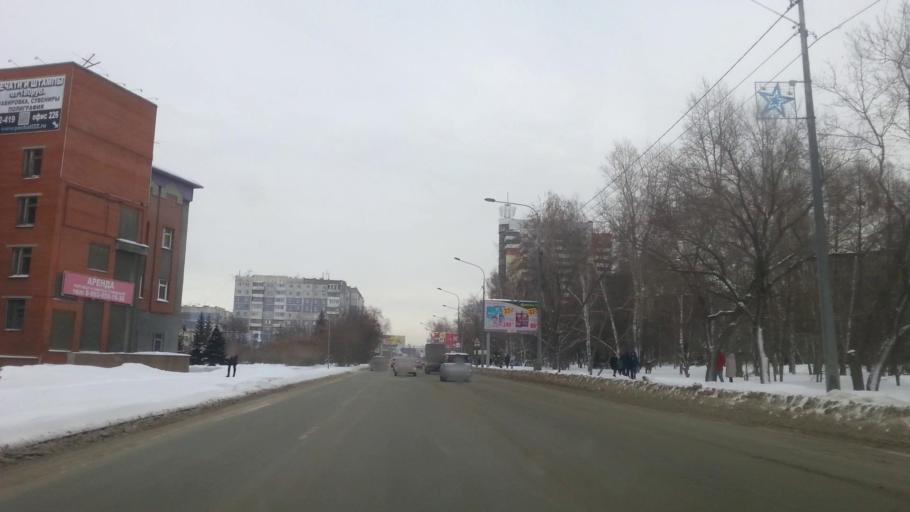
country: RU
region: Altai Krai
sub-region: Gorod Barnaulskiy
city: Barnaul
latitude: 53.3441
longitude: 83.7561
